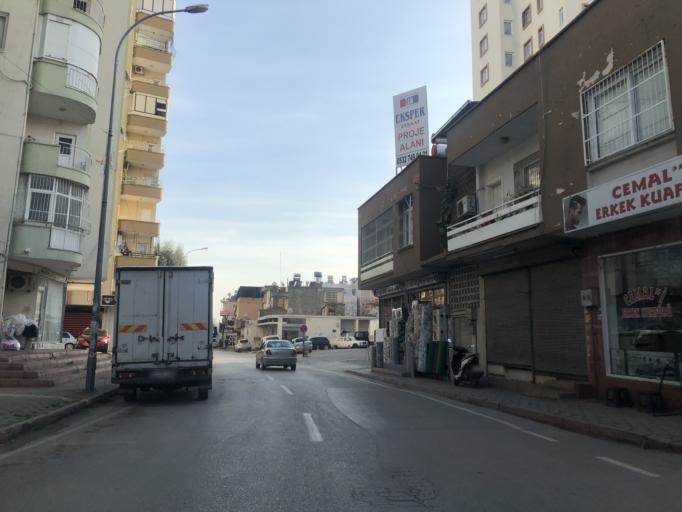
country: TR
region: Adana
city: Adana
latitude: 37.0187
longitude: 35.3142
